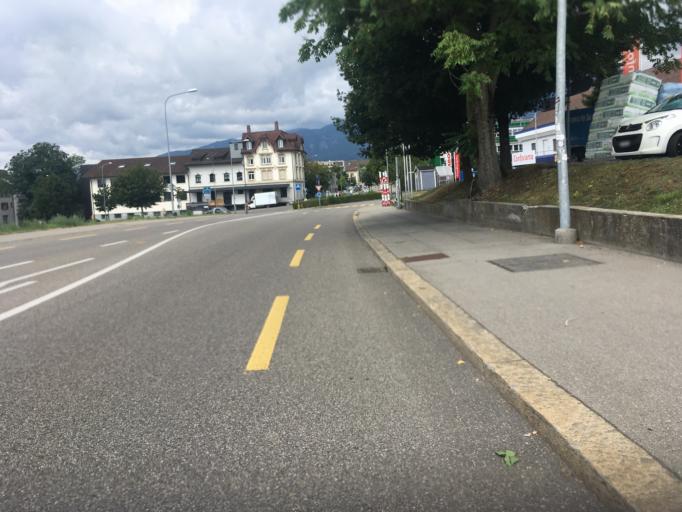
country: CH
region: Solothurn
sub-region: Bezirk Solothurn
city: Solothurn
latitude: 47.2106
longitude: 7.5276
